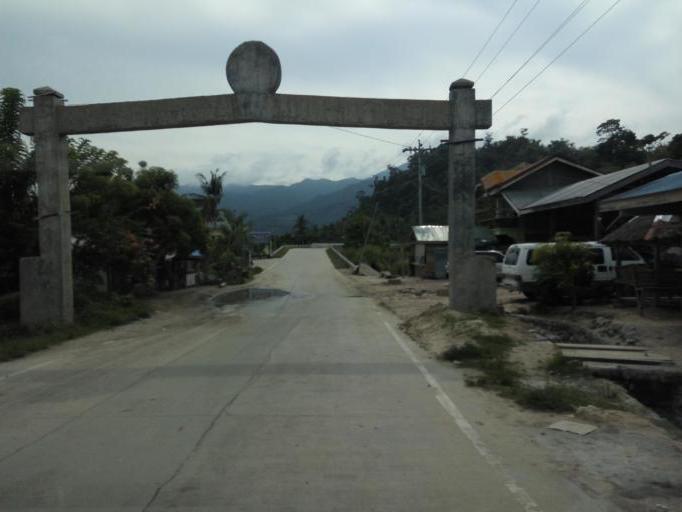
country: PH
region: Central Luzon
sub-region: Province of Aurora
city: Dinalongan
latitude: 16.0774
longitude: 121.7627
